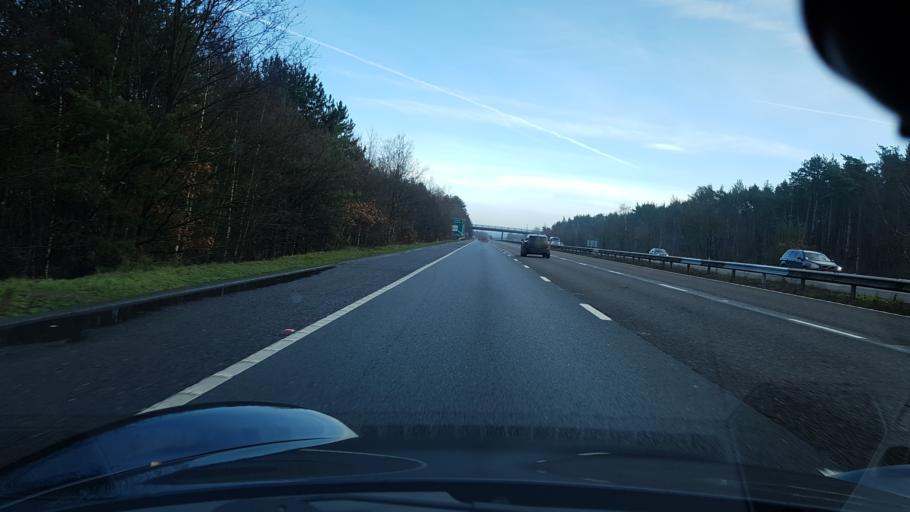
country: GB
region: England
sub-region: Surrey
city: Esher
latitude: 51.3460
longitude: -0.3761
